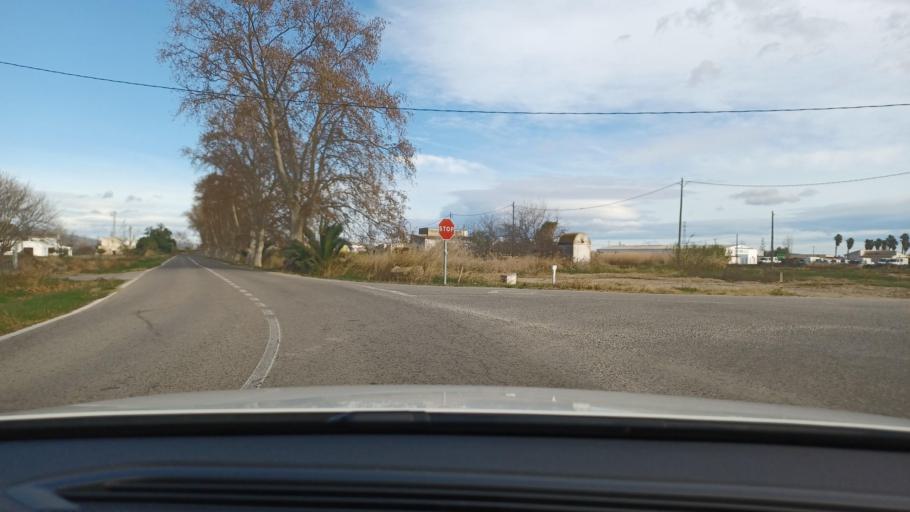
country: ES
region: Catalonia
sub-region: Provincia de Tarragona
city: Amposta
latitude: 40.7040
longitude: 0.5894
